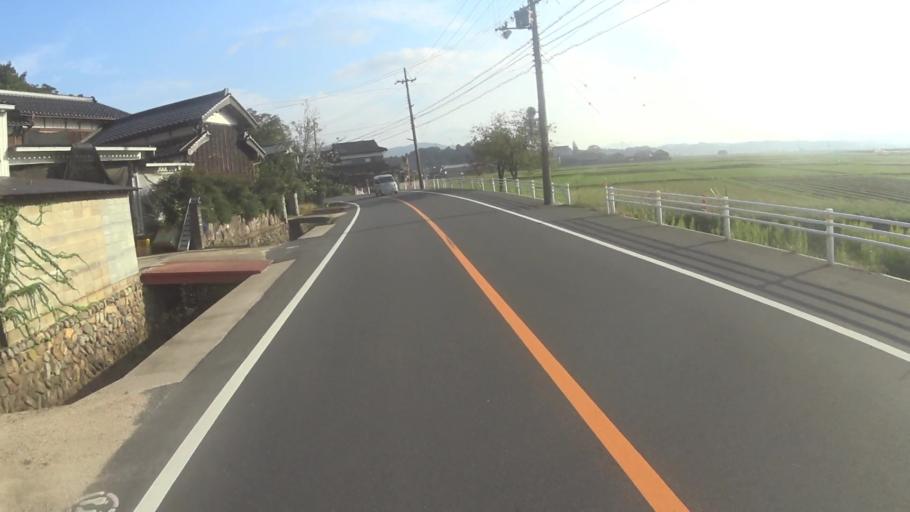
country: JP
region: Kyoto
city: Miyazu
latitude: 35.6854
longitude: 135.0985
